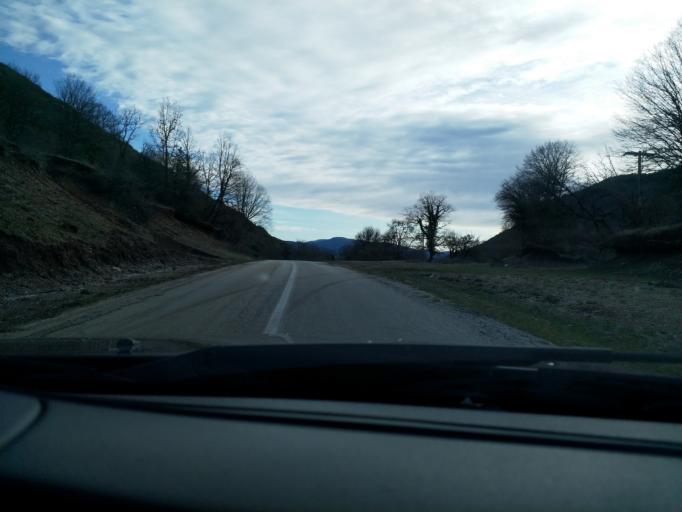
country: GR
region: Epirus
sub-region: Nomos Ioanninon
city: Asprangeloi
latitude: 39.8670
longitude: 20.7289
